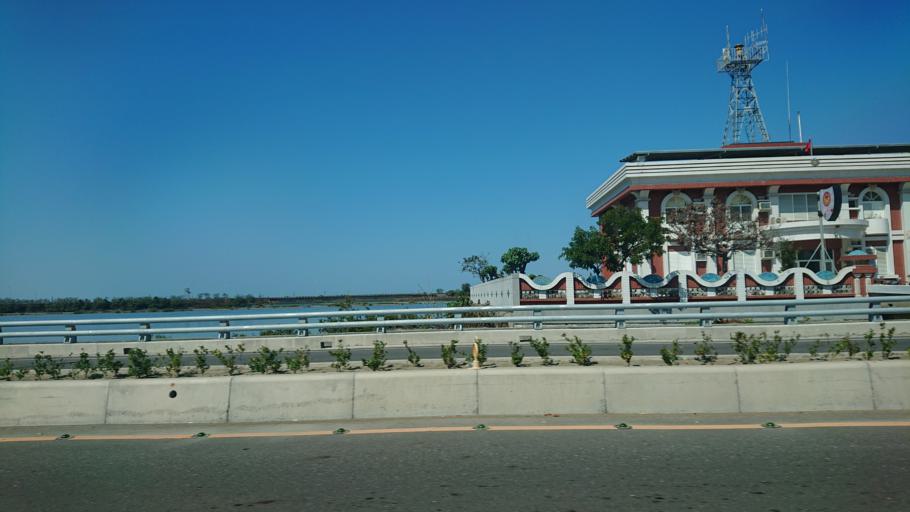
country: TW
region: Taiwan
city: Xinying
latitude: 23.2827
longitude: 120.1345
